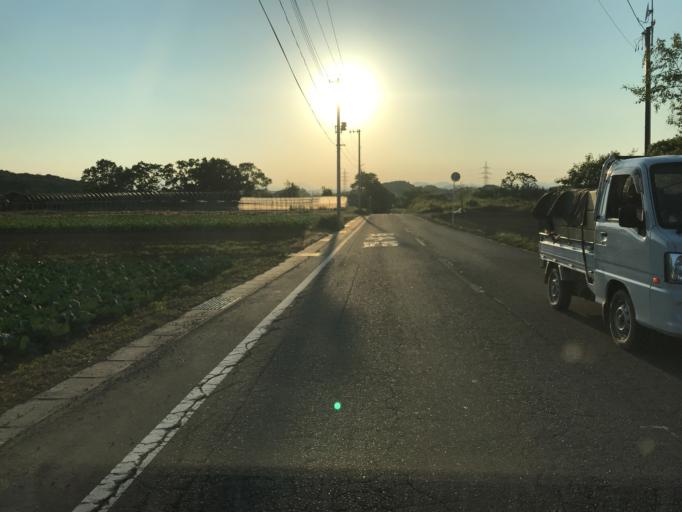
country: JP
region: Fukushima
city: Ishikawa
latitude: 37.1765
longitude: 140.3433
